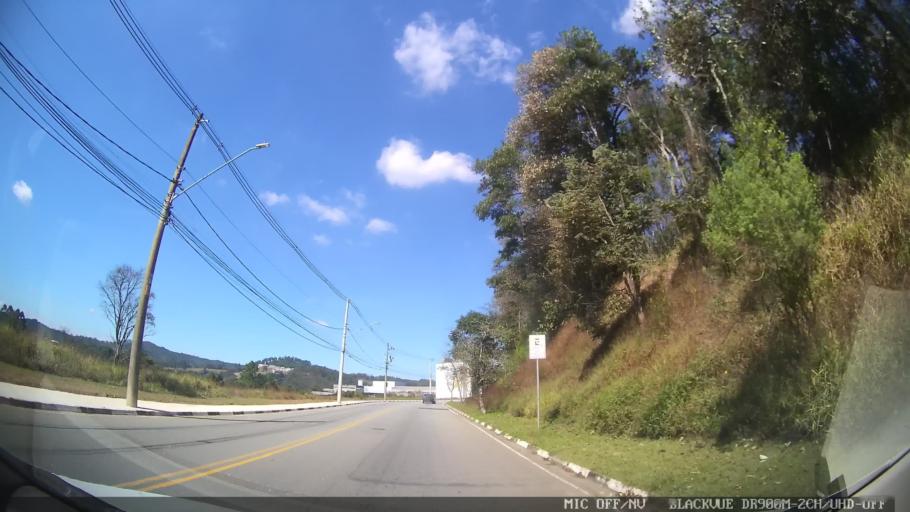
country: BR
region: Sao Paulo
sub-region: Carapicuiba
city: Carapicuiba
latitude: -23.4619
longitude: -46.8340
